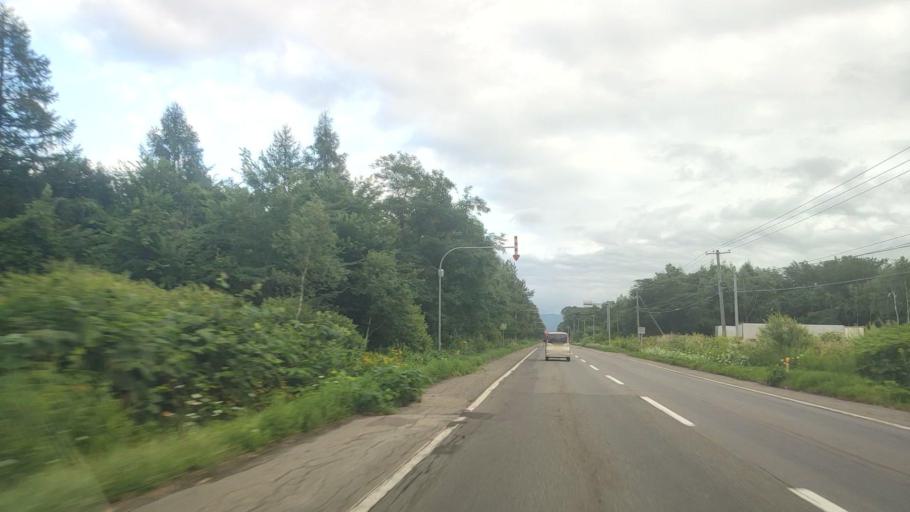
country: JP
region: Hokkaido
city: Nanae
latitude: 42.0209
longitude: 140.6169
